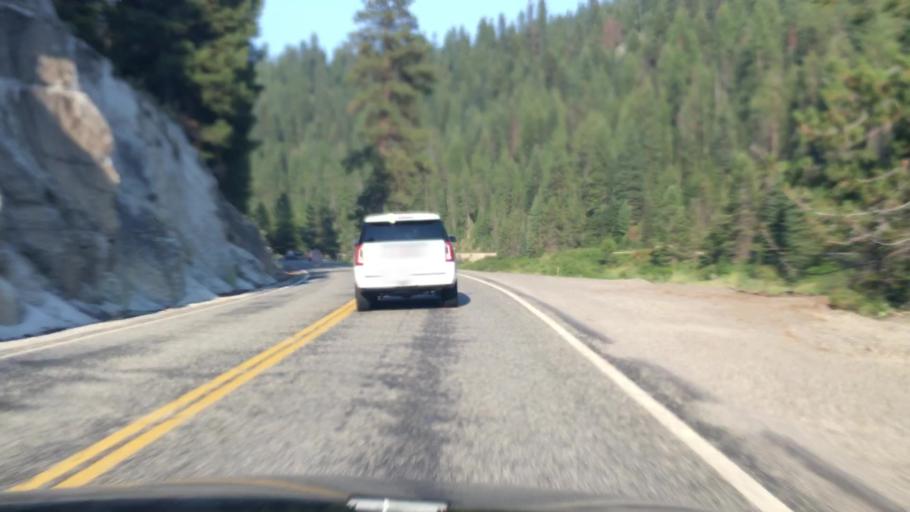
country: US
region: Idaho
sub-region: Valley County
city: Cascade
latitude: 44.3128
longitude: -116.0746
